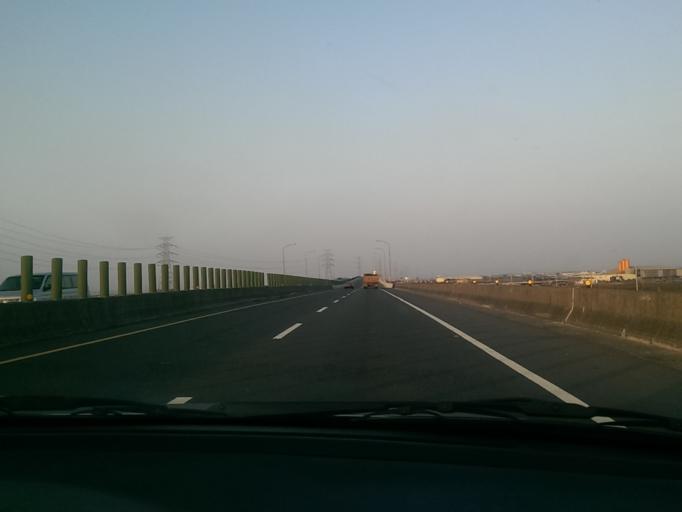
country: TW
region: Taiwan
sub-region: Changhua
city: Chang-hua
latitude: 24.1627
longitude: 120.4655
